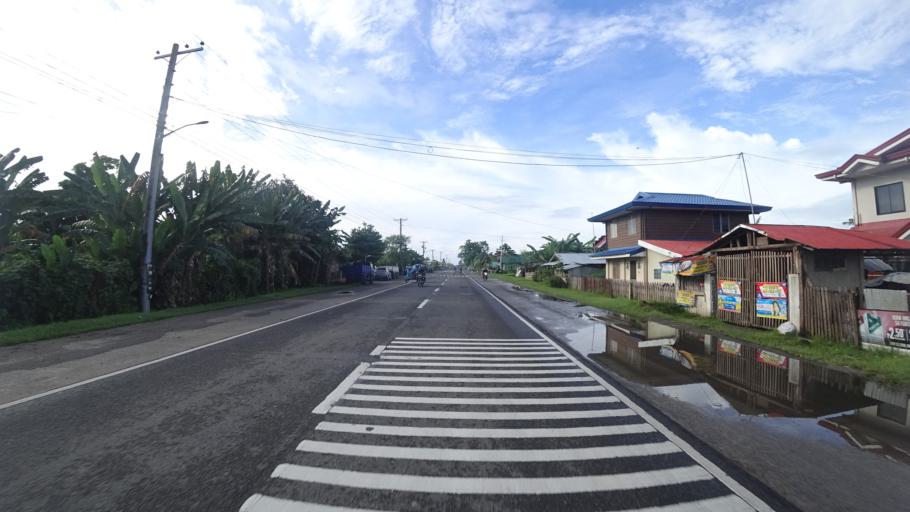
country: PH
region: Eastern Visayas
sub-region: Province of Leyte
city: Palo
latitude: 11.1489
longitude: 125.0007
